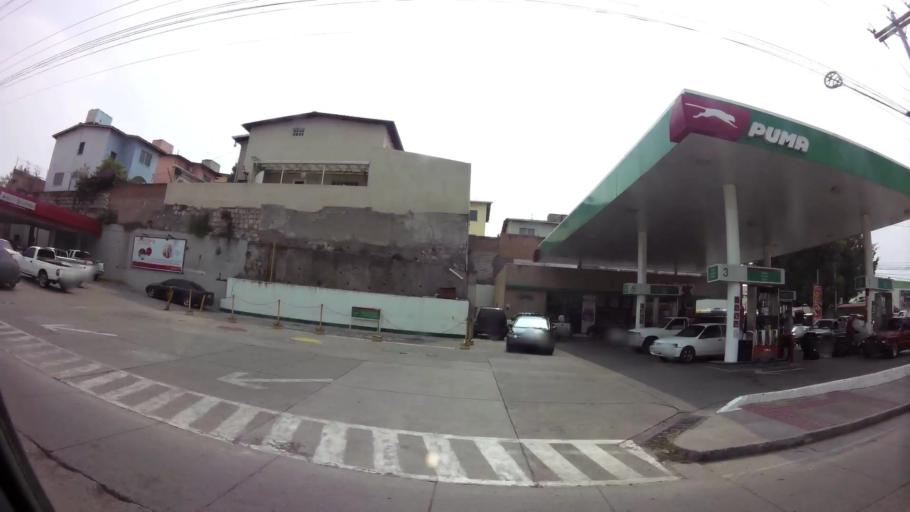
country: HN
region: Francisco Morazan
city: Tegucigalpa
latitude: 14.0671
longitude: -87.1841
